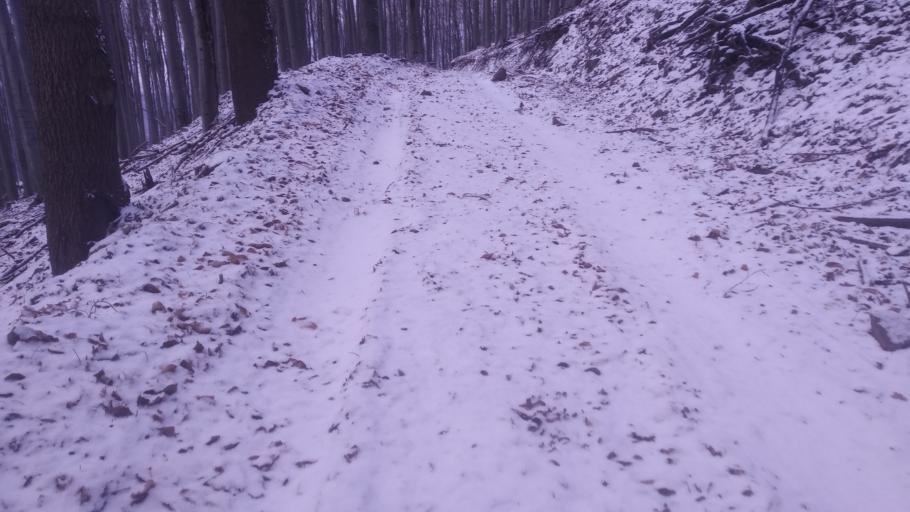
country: SK
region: Nitriansky
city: Sahy
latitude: 47.9679
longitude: 18.9282
